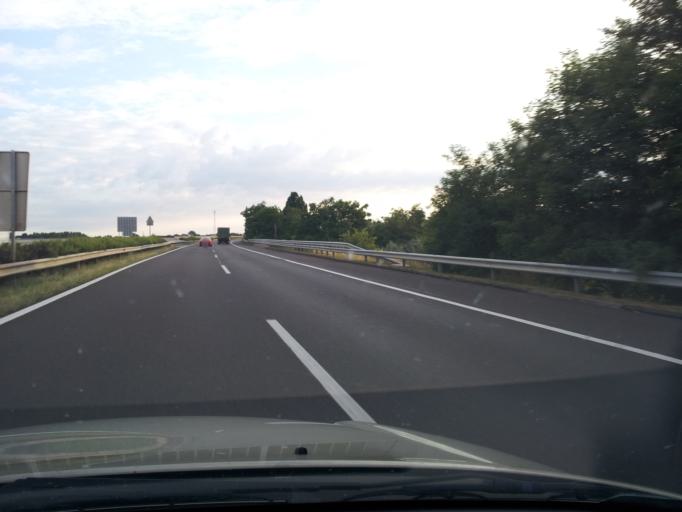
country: HU
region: Heves
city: Hatvan
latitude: 47.6850
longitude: 19.7306
